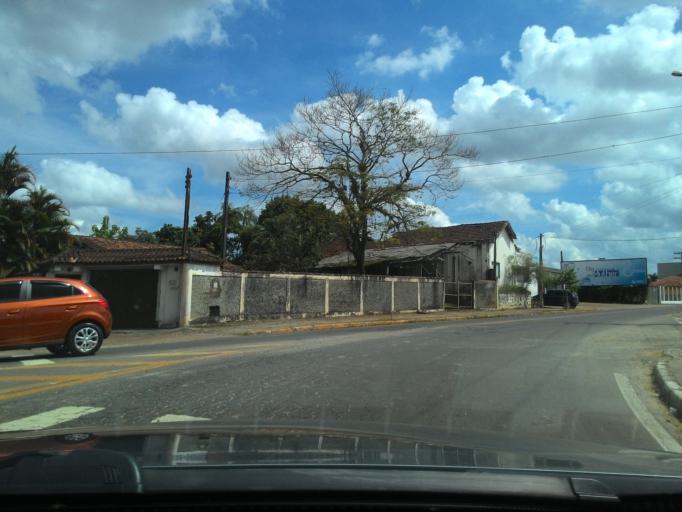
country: BR
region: Sao Paulo
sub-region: Registro
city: Registro
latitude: -24.5023
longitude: -47.8545
